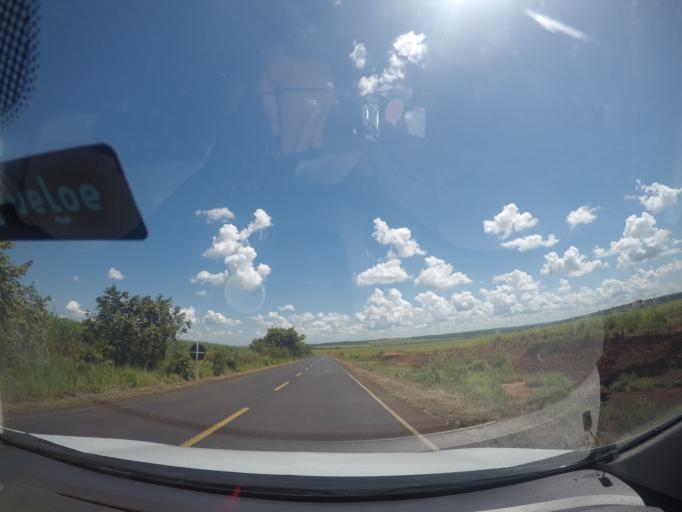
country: BR
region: Minas Gerais
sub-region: Frutal
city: Frutal
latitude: -19.7020
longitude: -48.7674
